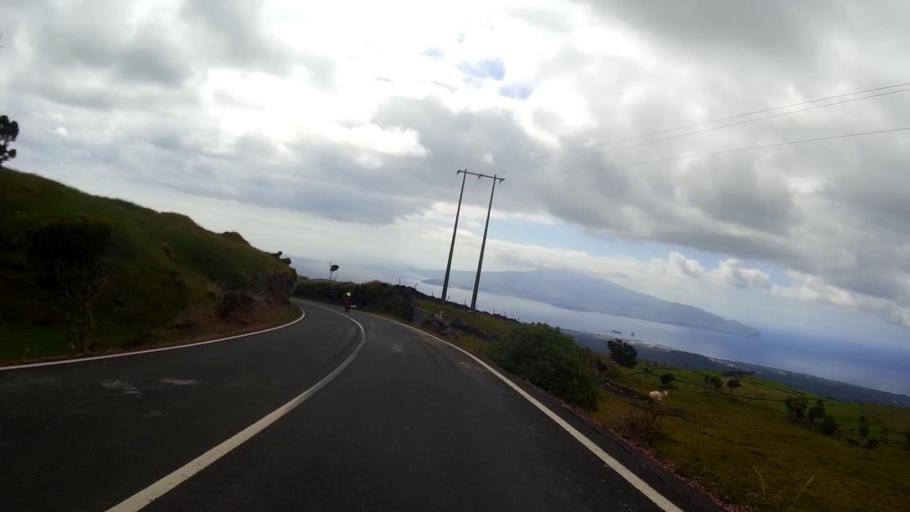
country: PT
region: Azores
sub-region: Madalena
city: Madalena
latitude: 38.4966
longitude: -28.4435
